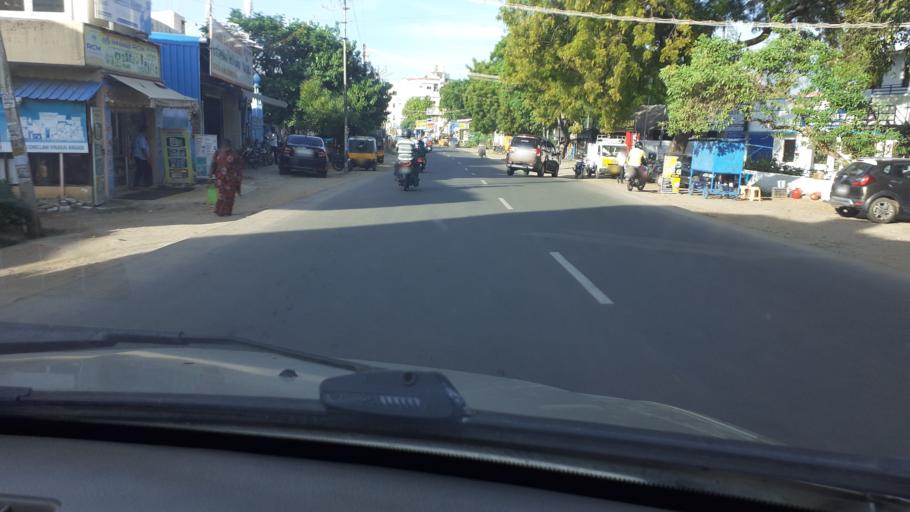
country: IN
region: Tamil Nadu
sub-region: Tirunelveli Kattabo
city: Tirunelveli
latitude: 8.7121
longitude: 77.7316
